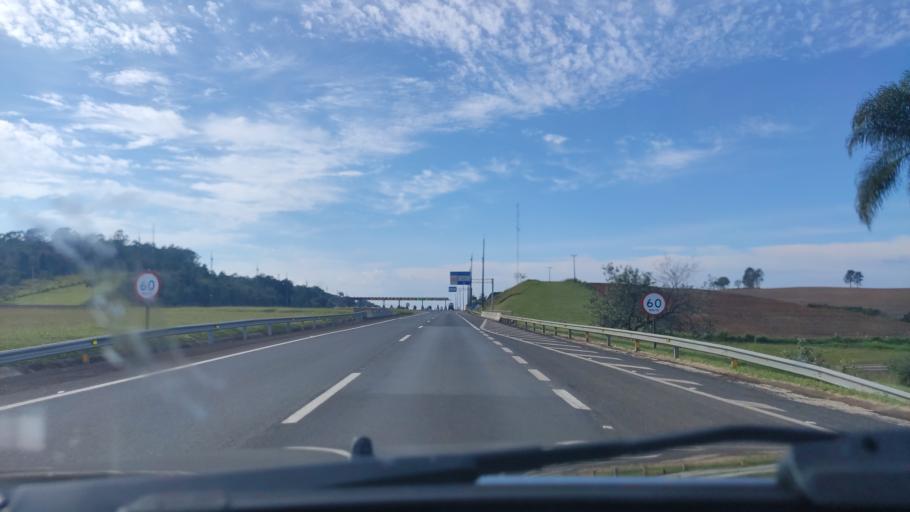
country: BR
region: Sao Paulo
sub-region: Itatinga
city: Itatinga
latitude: -23.0803
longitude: -48.5189
